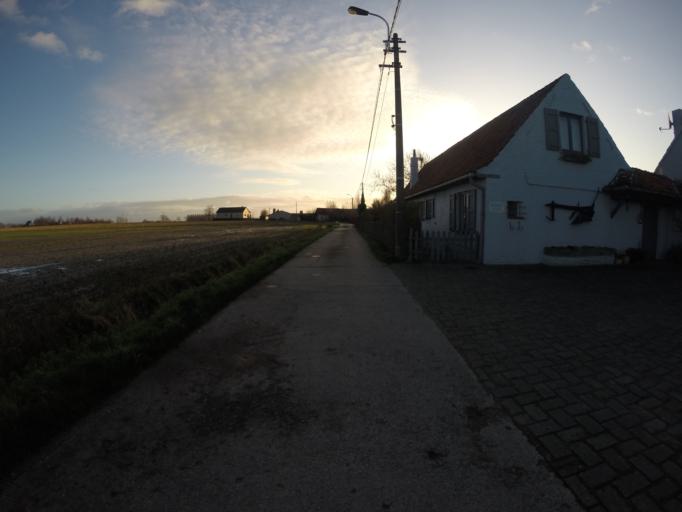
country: BE
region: Flanders
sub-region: Provincie Oost-Vlaanderen
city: Nevele
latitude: 51.0396
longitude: 3.4921
